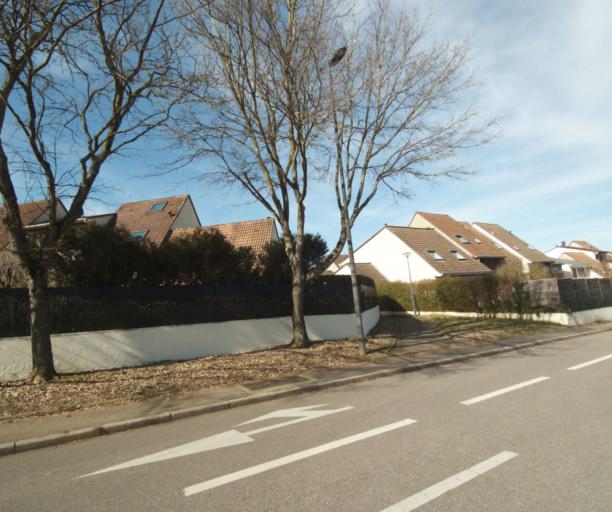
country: FR
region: Lorraine
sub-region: Departement de Meurthe-et-Moselle
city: Villers-les-Nancy
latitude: 48.6636
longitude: 6.1555
